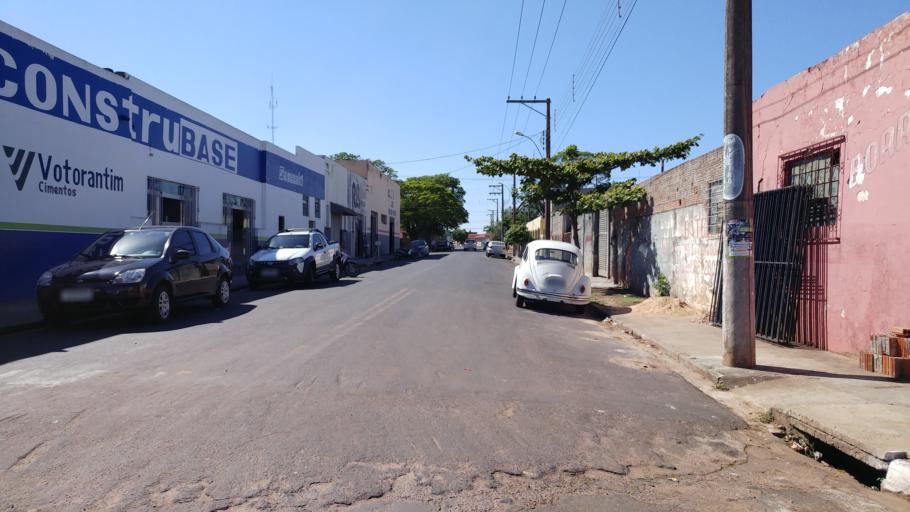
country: BR
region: Sao Paulo
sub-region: Paraguacu Paulista
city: Paraguacu Paulista
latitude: -22.4270
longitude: -50.5838
